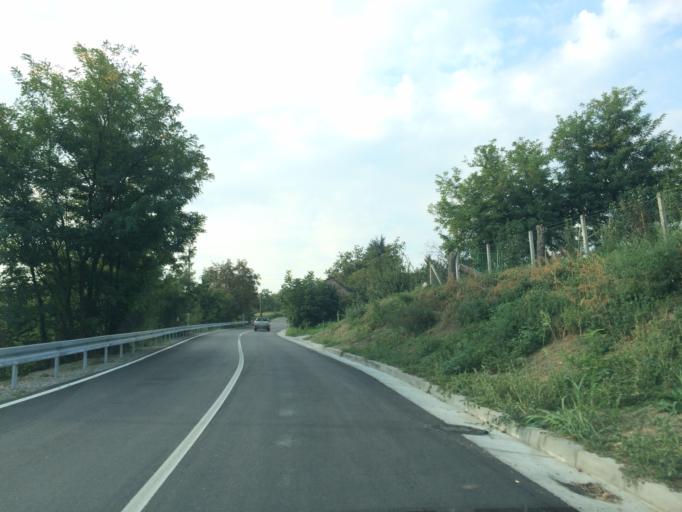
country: RS
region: Autonomna Pokrajina Vojvodina
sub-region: Juznobacki Okrug
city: Novi Sad
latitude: 45.2095
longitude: 19.8056
